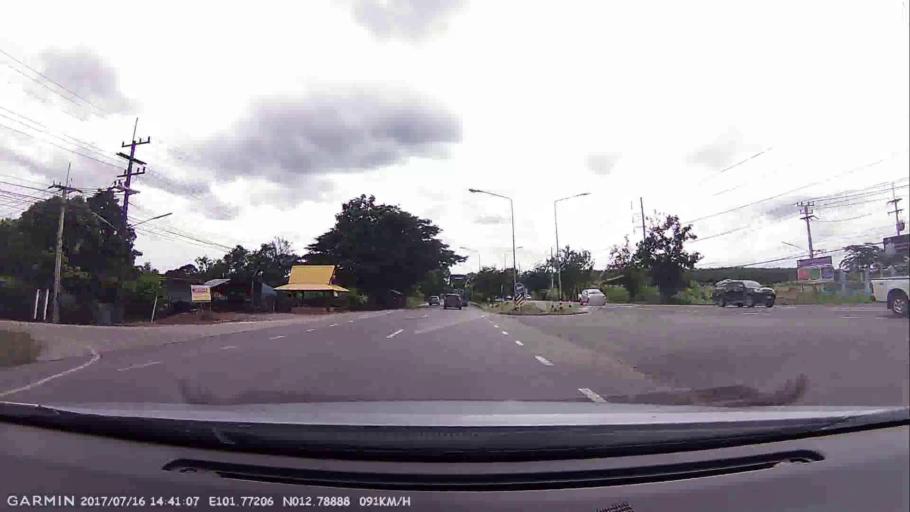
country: TH
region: Chanthaburi
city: Na Yai Am
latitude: 12.7889
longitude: 101.7718
